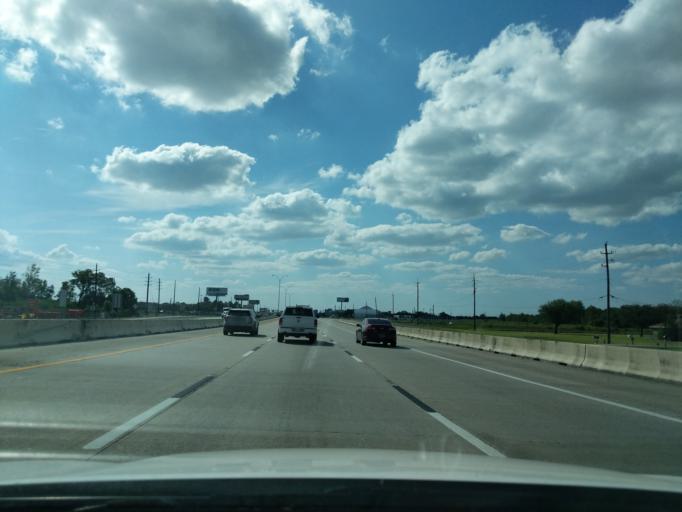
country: US
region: Texas
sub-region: Chambers County
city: Mont Belvieu
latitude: 29.8242
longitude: -94.8695
